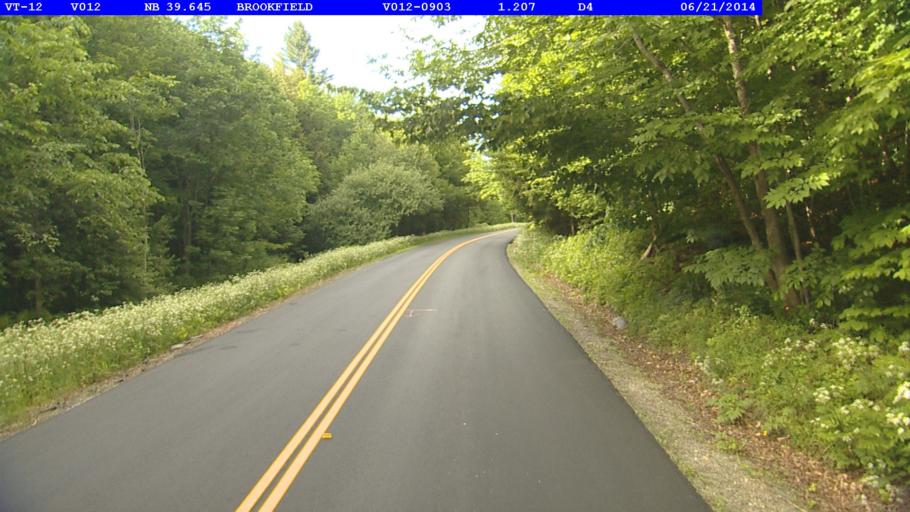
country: US
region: Vermont
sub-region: Orange County
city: Randolph
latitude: 44.0217
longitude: -72.6567
